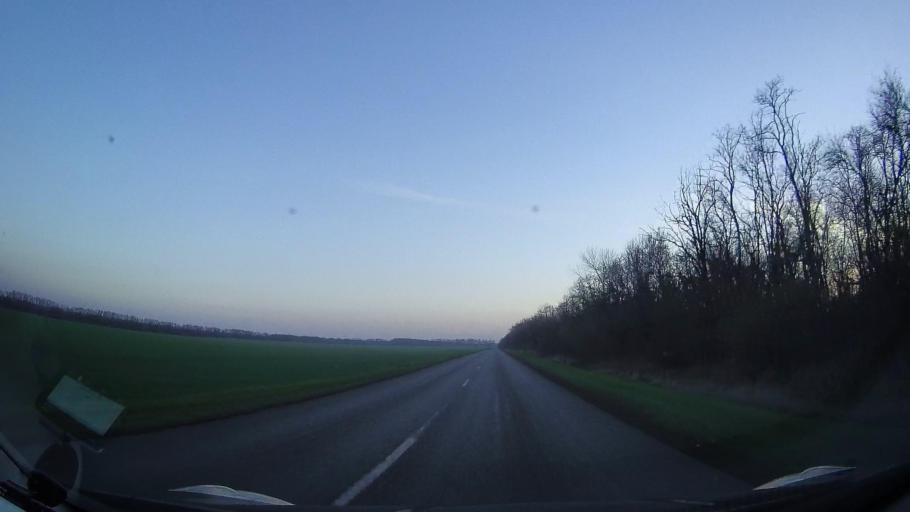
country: RU
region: Rostov
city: Zernograd
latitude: 46.9773
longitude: 40.3915
